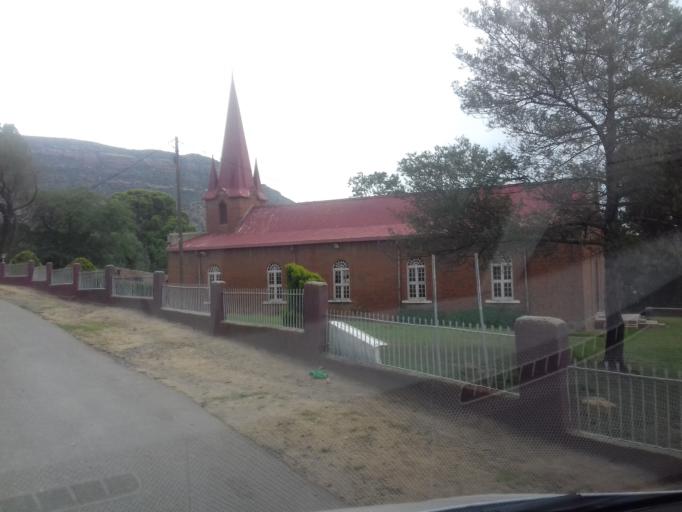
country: LS
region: Maseru
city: Nako
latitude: -29.6250
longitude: 27.5084
